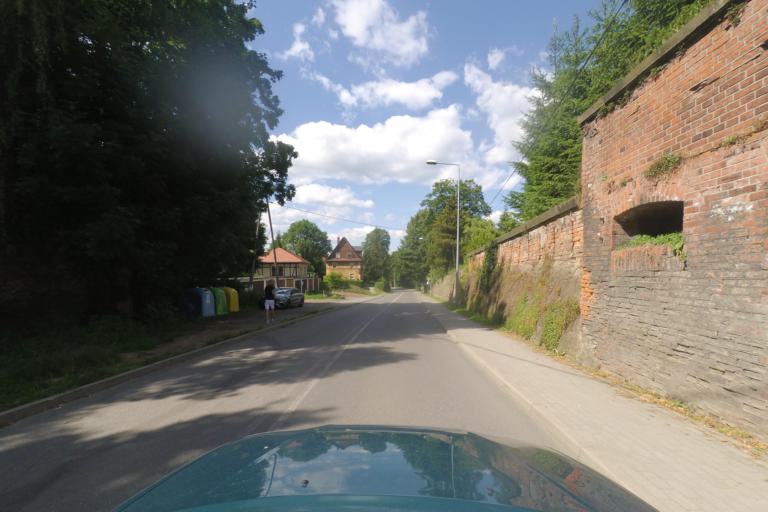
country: PL
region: Lower Silesian Voivodeship
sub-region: Powiat klodzki
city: Klodzko
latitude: 50.4436
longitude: 16.6569
